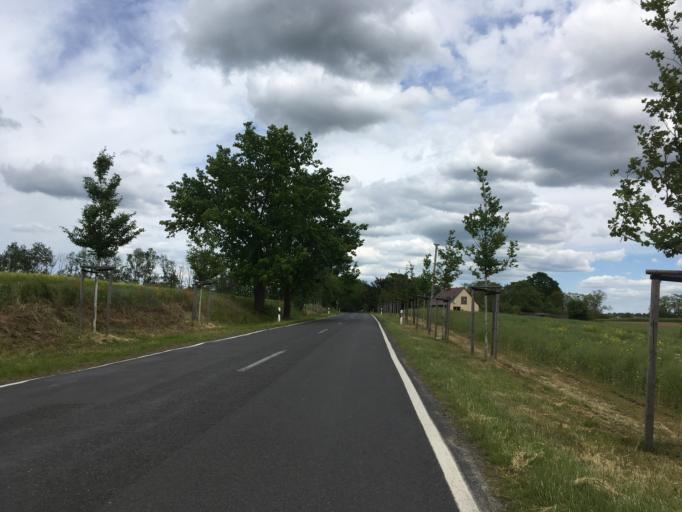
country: DE
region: Brandenburg
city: Hohenfinow
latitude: 52.7667
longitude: 13.8874
